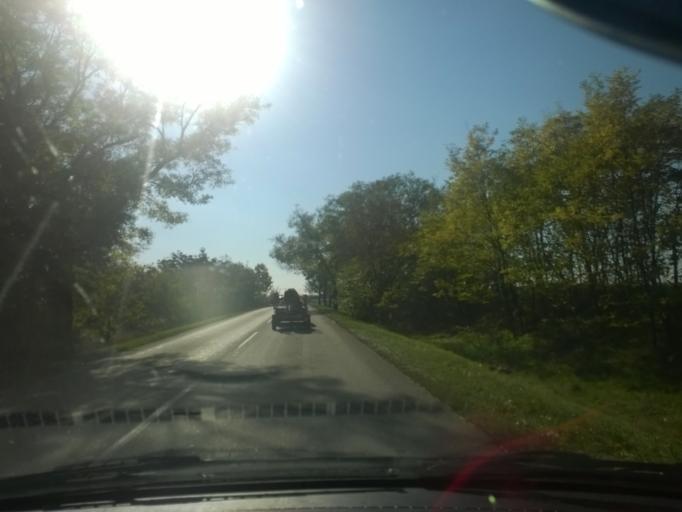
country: HU
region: Csongrad
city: Szegvar
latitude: 46.5394
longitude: 20.3162
